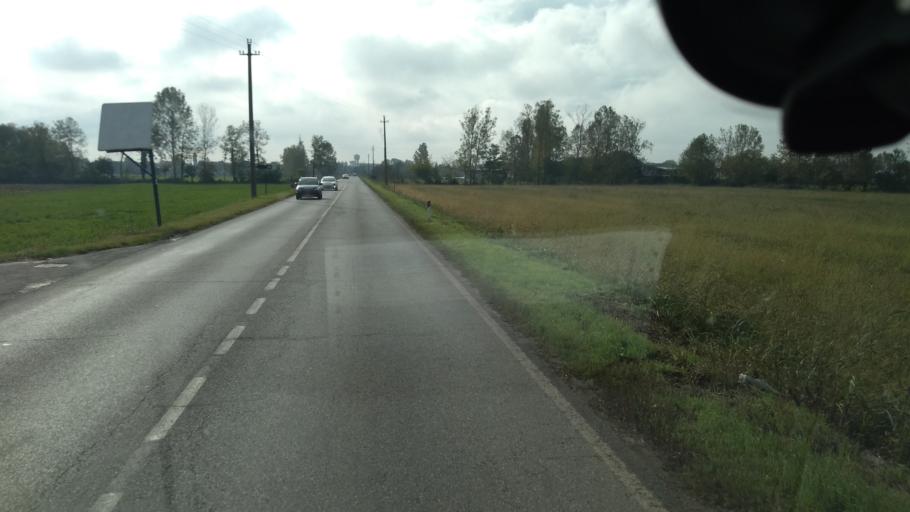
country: IT
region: Lombardy
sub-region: Provincia di Bergamo
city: Vidalengo
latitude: 45.5304
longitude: 9.6389
